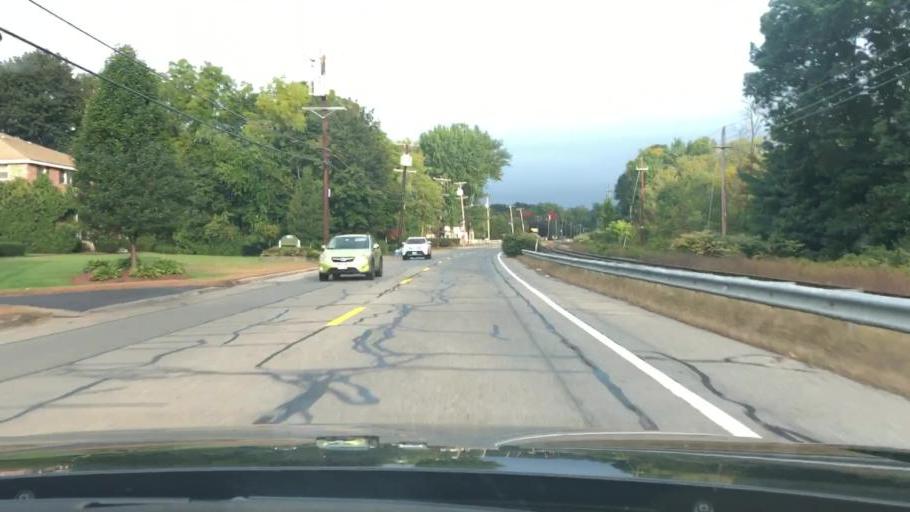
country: US
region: Massachusetts
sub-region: Middlesex County
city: Tyngsboro
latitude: 42.6462
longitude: -71.3941
